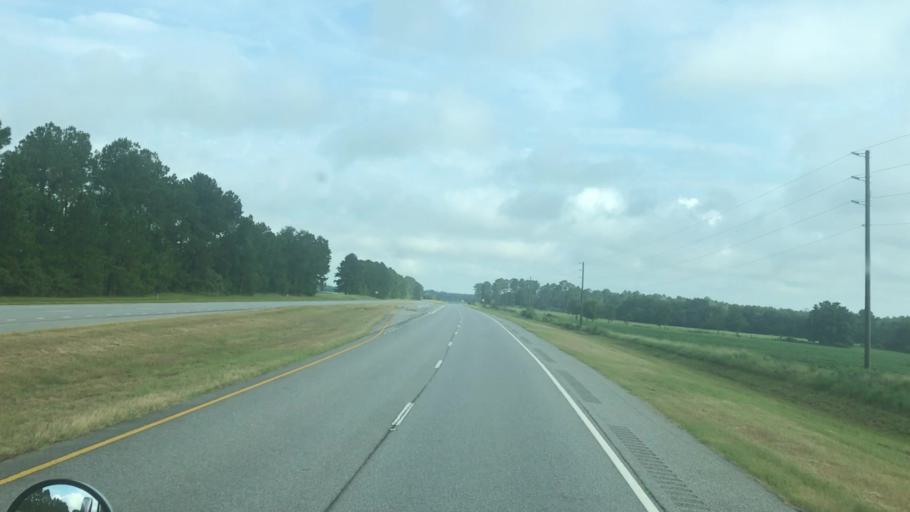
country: US
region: Georgia
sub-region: Miller County
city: Colquitt
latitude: 31.2066
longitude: -84.7721
